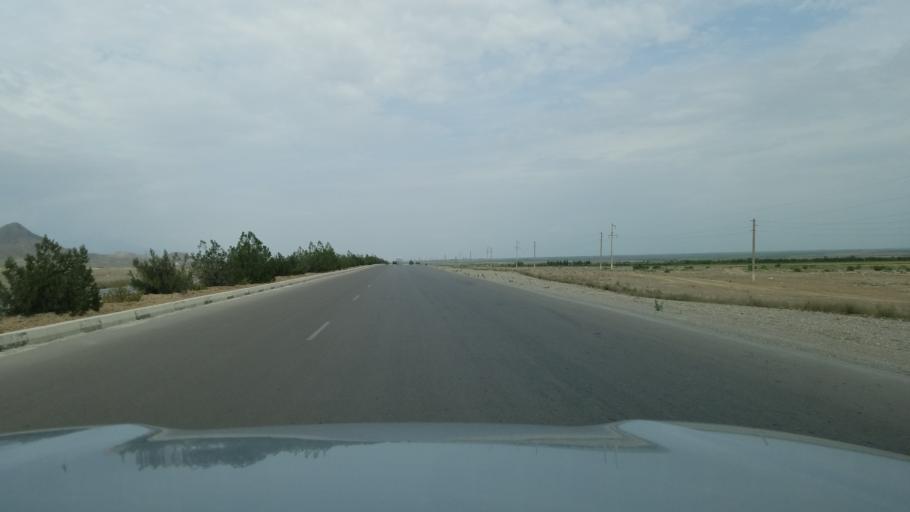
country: TM
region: Ahal
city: Baharly
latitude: 38.2318
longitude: 57.7836
